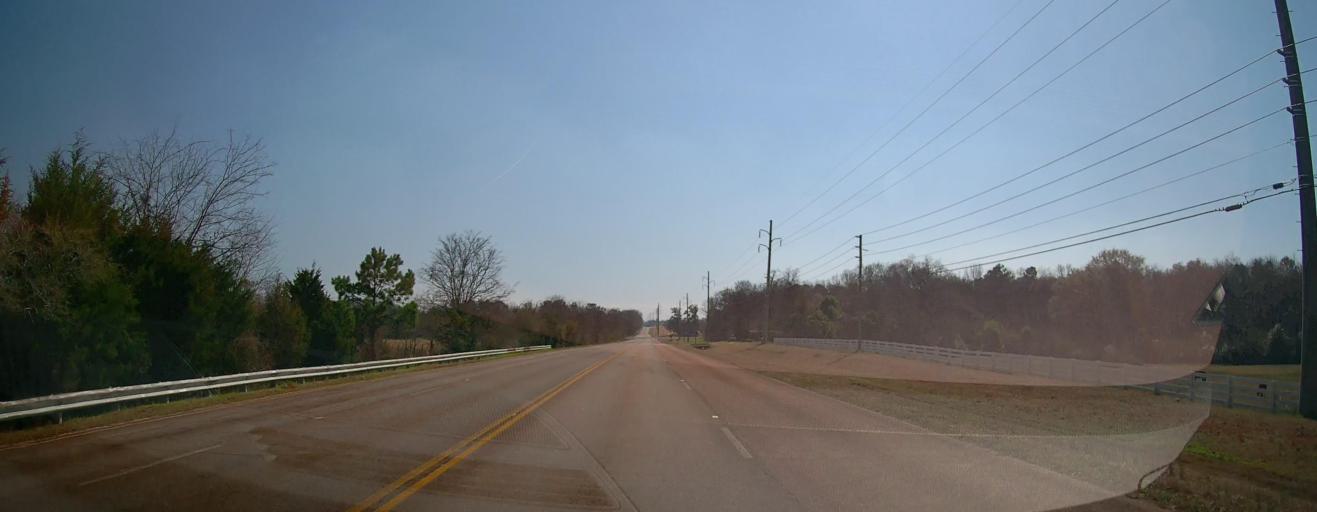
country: US
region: Georgia
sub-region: Houston County
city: Perry
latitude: 32.4853
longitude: -83.7588
